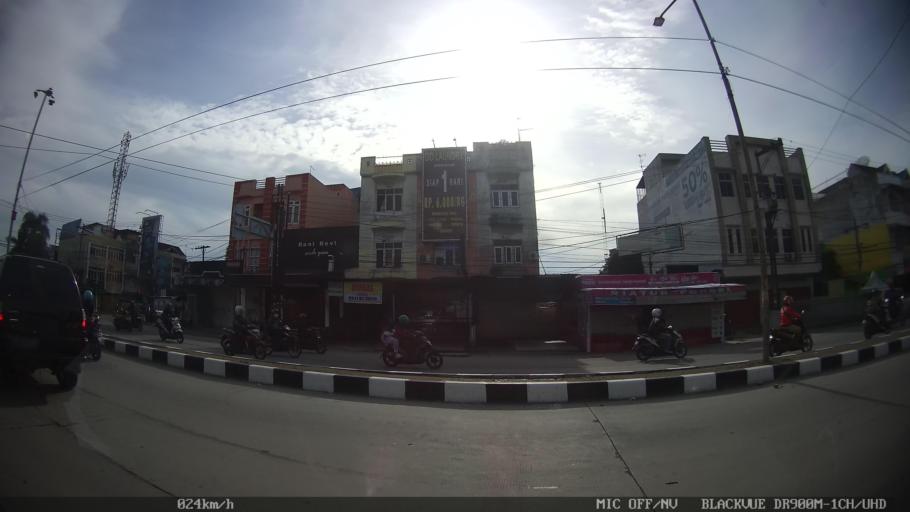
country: ID
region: North Sumatra
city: Medan
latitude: 3.6042
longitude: 98.6459
